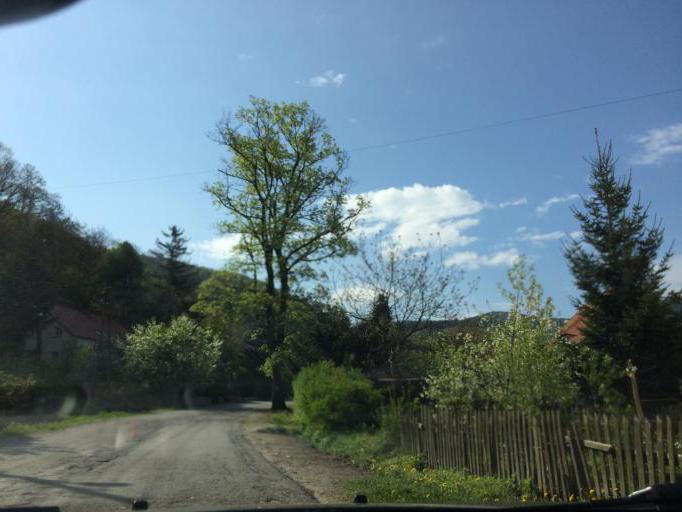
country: PL
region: Lower Silesian Voivodeship
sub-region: Powiat dzierzoniowski
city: Pieszyce
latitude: 50.6777
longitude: 16.5440
